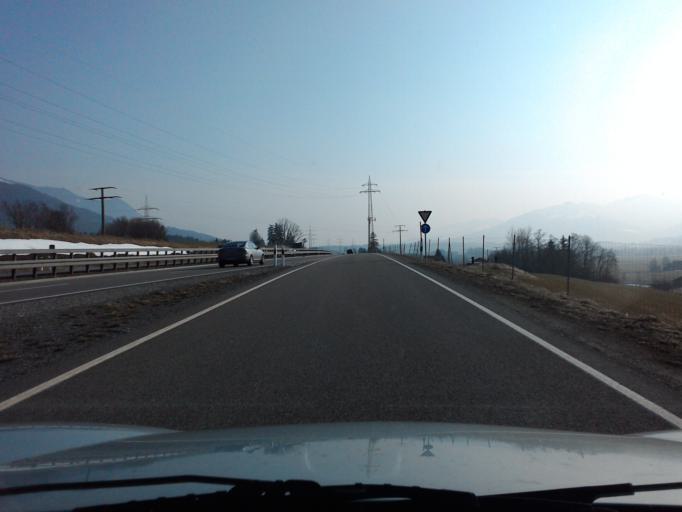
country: DE
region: Bavaria
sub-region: Swabia
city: Rettenberg
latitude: 47.6126
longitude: 10.2741
